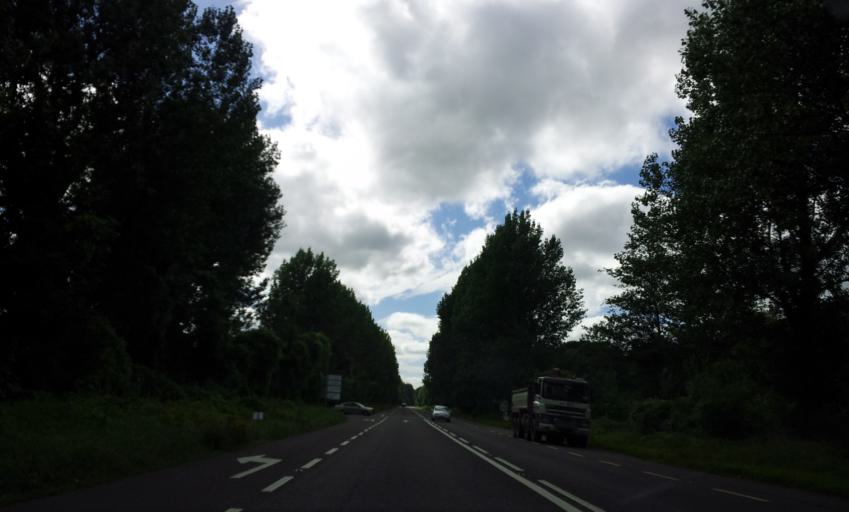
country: IE
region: Munster
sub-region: County Cork
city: Bandon
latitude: 51.8551
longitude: -8.8107
